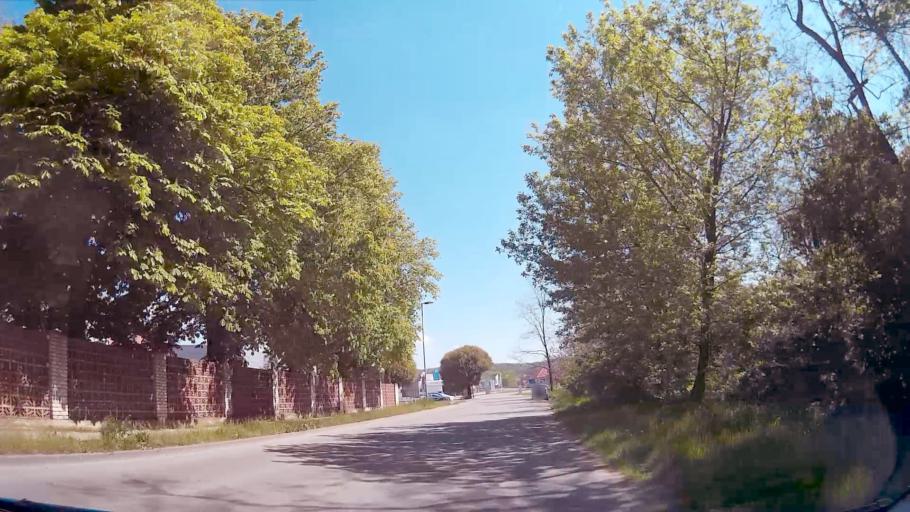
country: CZ
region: South Moravian
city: Ivancice
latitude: 49.0952
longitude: 16.3659
